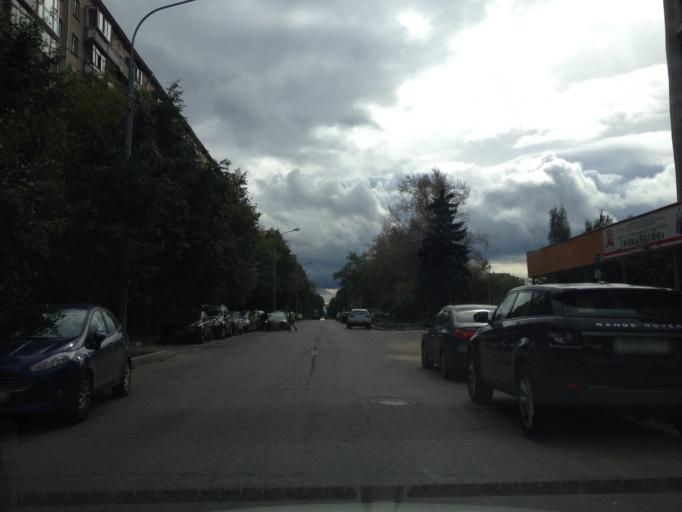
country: RU
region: Moscow
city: Metrogorodok
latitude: 55.8062
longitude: 37.8049
